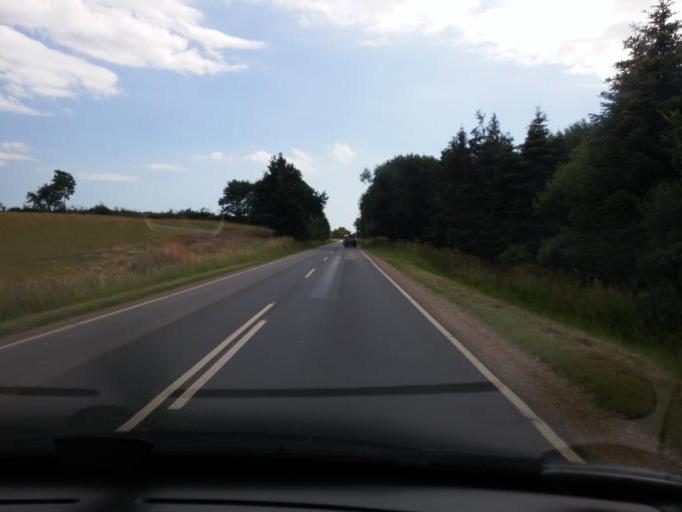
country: DK
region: South Denmark
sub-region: Langeland Kommune
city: Rudkobing
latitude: 54.9002
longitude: 10.7380
